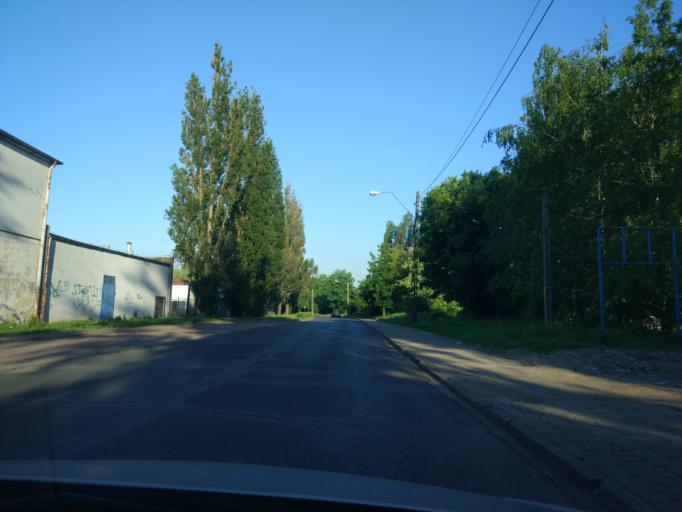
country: PL
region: Lodz Voivodeship
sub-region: Powiat kutnowski
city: Kutno
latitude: 52.2258
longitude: 19.3551
